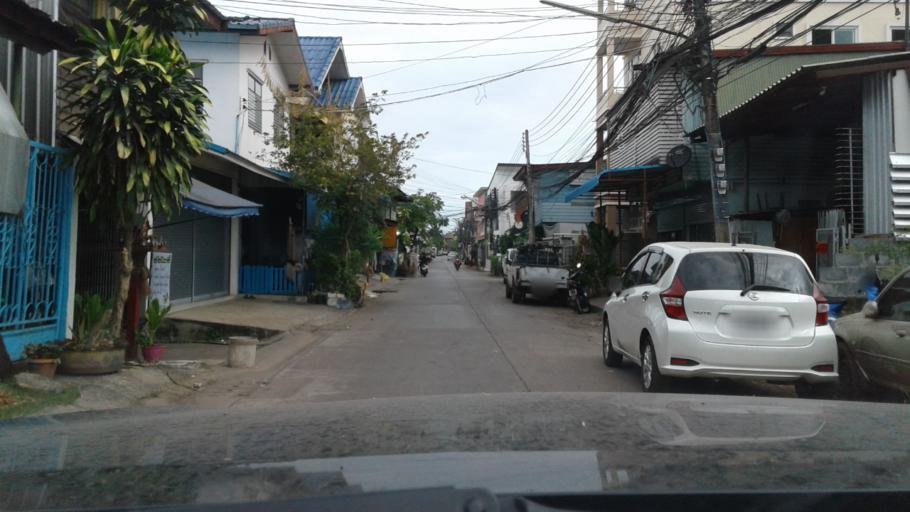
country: TH
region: Changwat Udon Thani
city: Udon Thani
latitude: 17.4083
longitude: 102.8025
